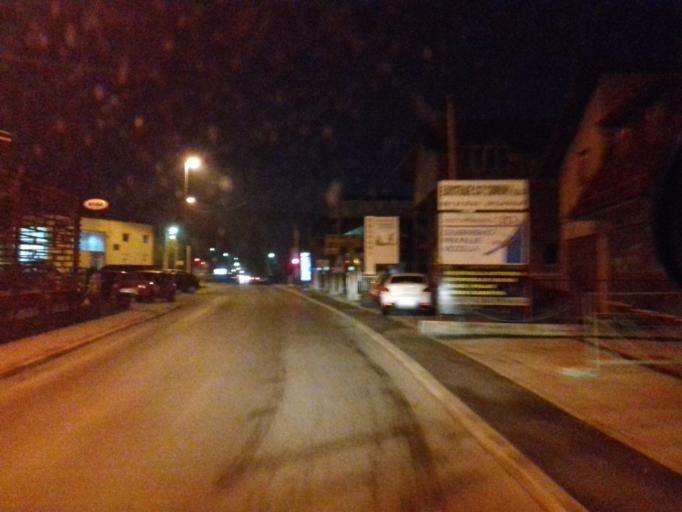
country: BA
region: Federation of Bosnia and Herzegovina
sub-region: Kanton Sarajevo
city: Sarajevo
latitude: 43.8416
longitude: 18.3381
